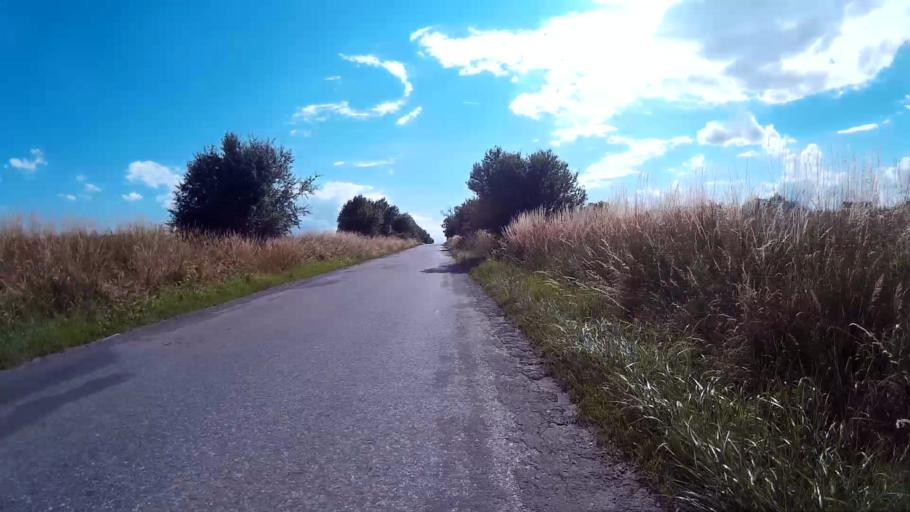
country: CZ
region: South Moravian
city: Troubsko
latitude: 49.1591
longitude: 16.5193
